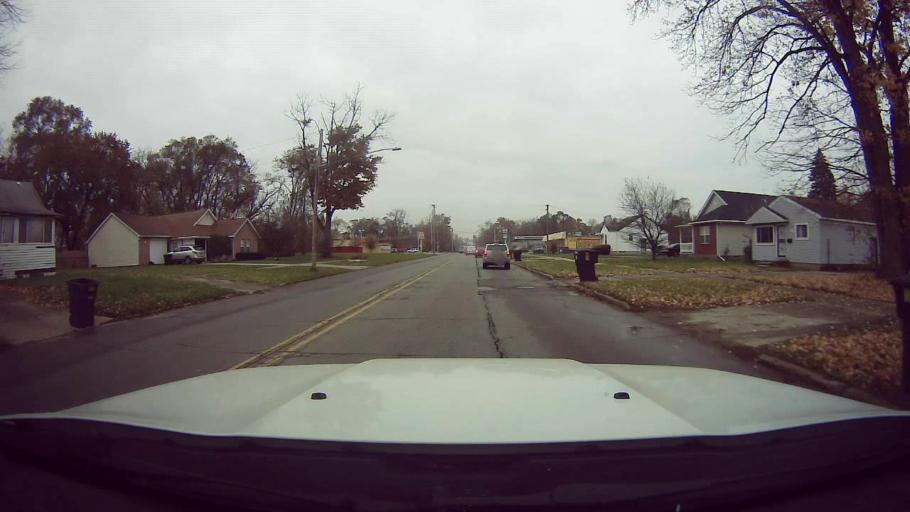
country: US
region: Michigan
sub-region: Wayne County
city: Redford
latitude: 42.3990
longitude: -83.2567
